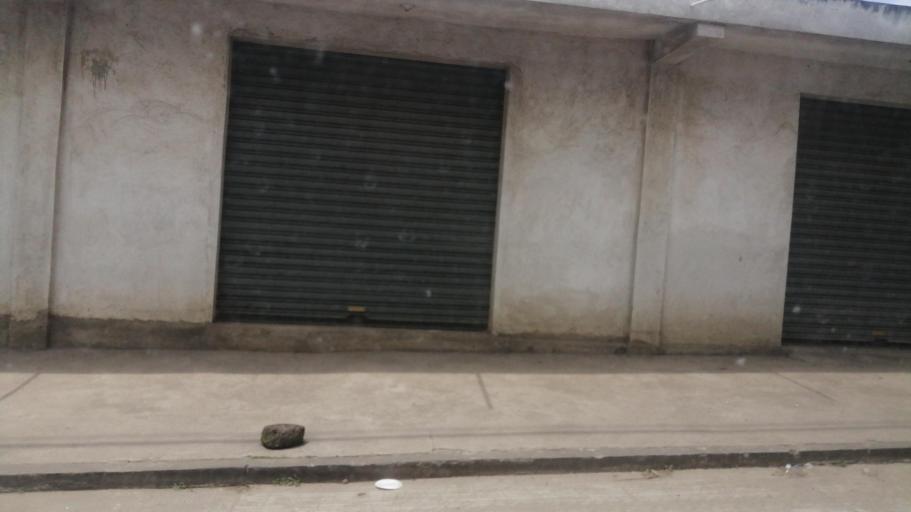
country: GT
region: Quetzaltenango
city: Cantel
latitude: 14.8182
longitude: -91.4348
